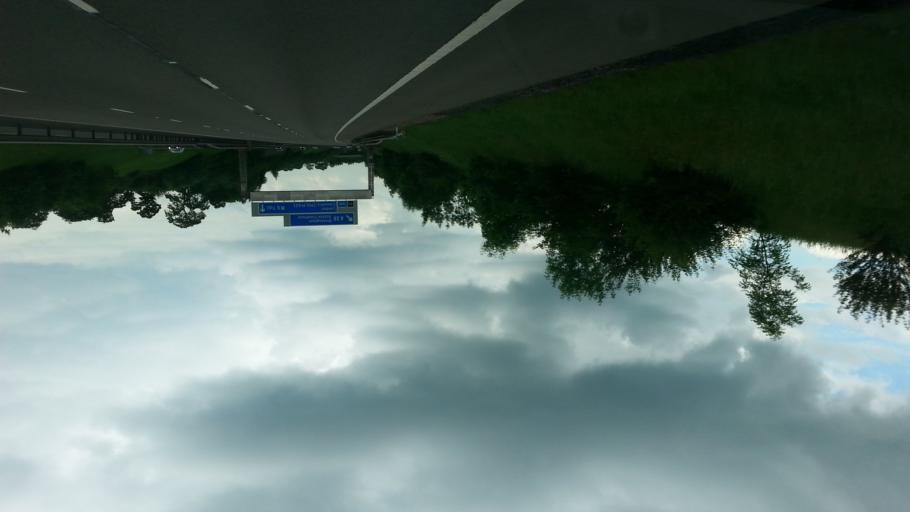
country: GB
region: England
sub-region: City and Borough of Birmingham
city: Sutton Coldfield
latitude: 52.5904
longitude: -1.7946
